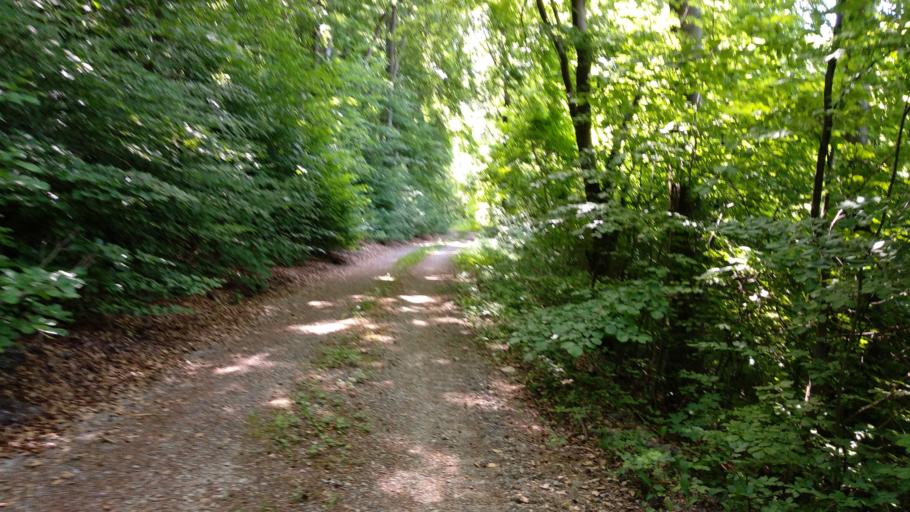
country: DE
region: North Rhine-Westphalia
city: Beverungen
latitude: 51.6481
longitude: 9.3567
